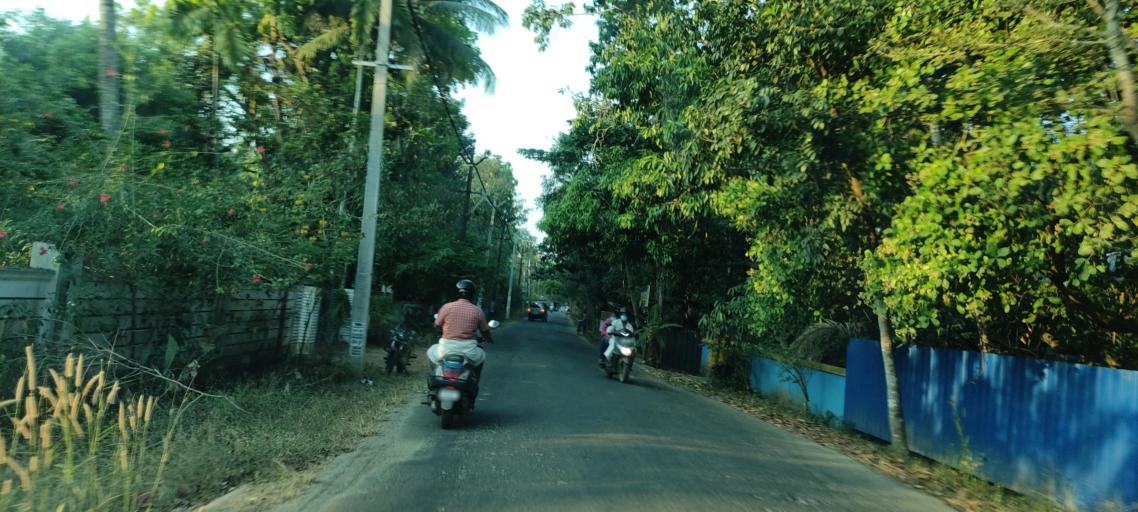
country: IN
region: Kerala
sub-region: Alappuzha
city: Kutiatodu
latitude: 9.7674
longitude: 76.3533
